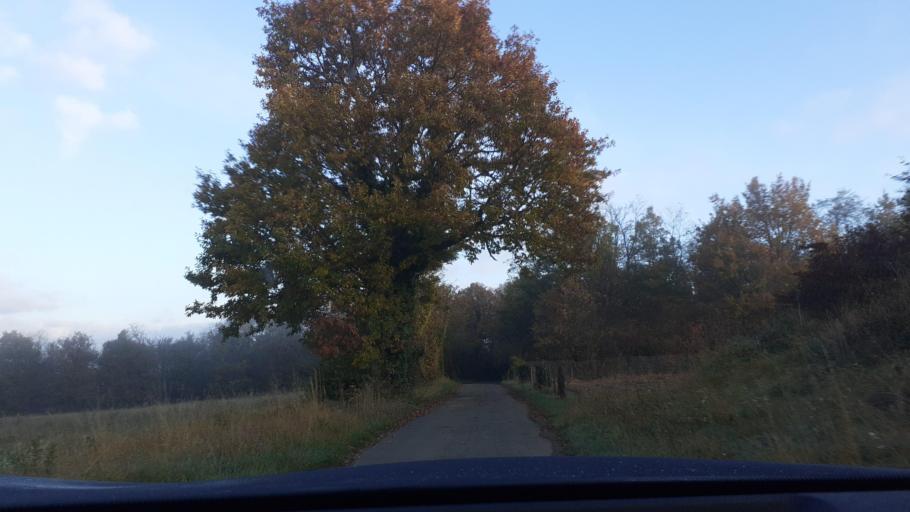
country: FR
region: Rhone-Alpes
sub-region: Departement du Rhone
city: Charnay
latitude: 45.9139
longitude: 4.6671
